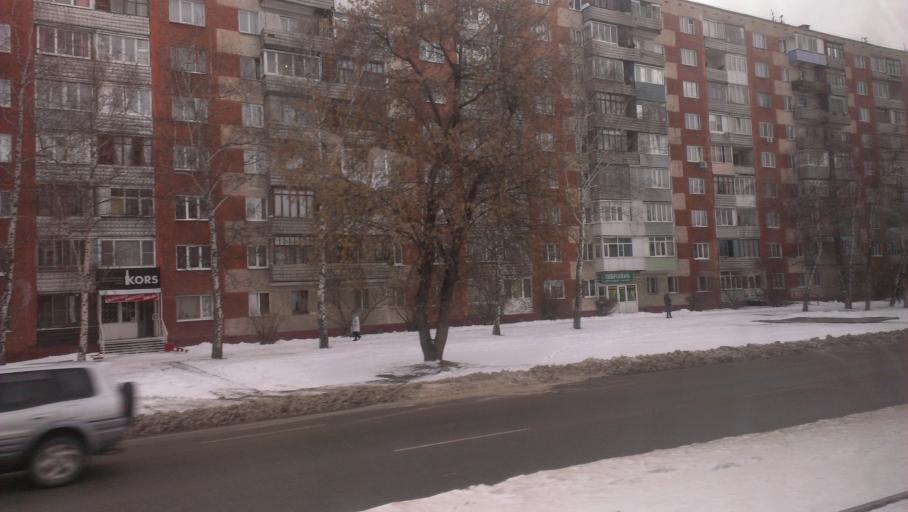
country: RU
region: Altai Krai
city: Novosilikatnyy
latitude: 53.3682
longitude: 83.6771
